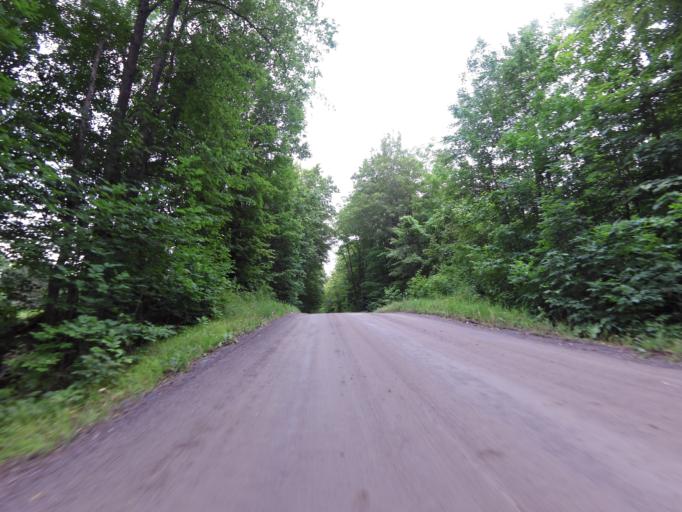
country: CA
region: Ontario
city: Kingston
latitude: 44.5548
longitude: -76.6267
